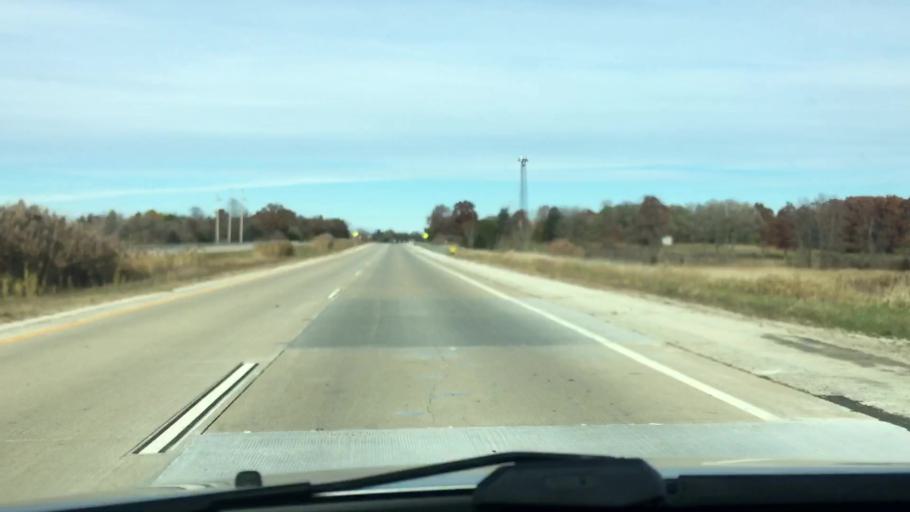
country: US
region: Wisconsin
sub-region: Brown County
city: Bellevue
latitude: 44.5912
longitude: -87.8647
